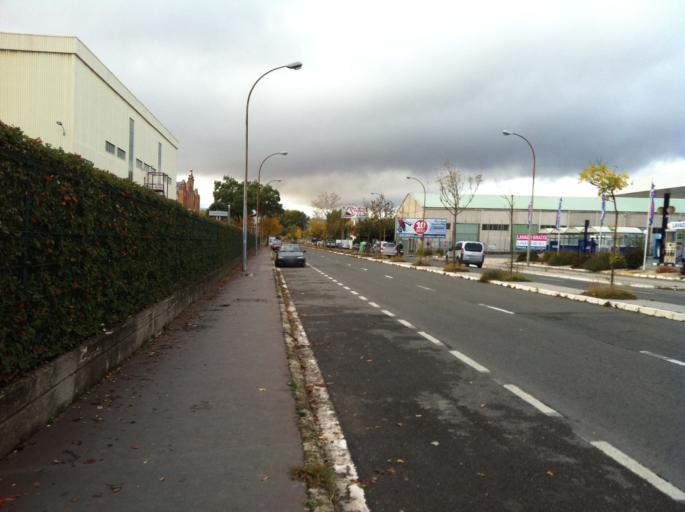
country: ES
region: Basque Country
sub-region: Provincia de Alava
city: Gasteiz / Vitoria
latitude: 42.8569
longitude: -2.7159
